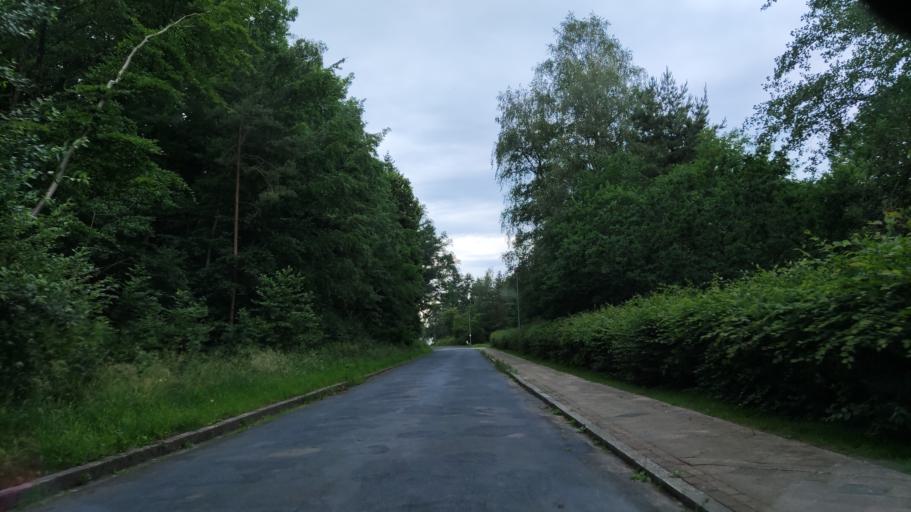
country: DE
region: Lower Saxony
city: Tosterglope
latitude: 53.2626
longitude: 10.8105
